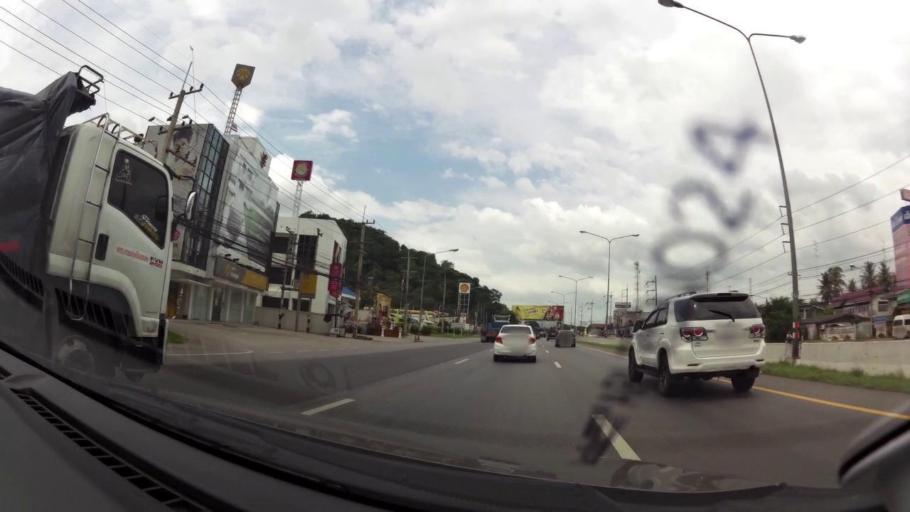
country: TH
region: Phetchaburi
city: Khao Yoi
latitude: 13.2408
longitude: 99.8239
